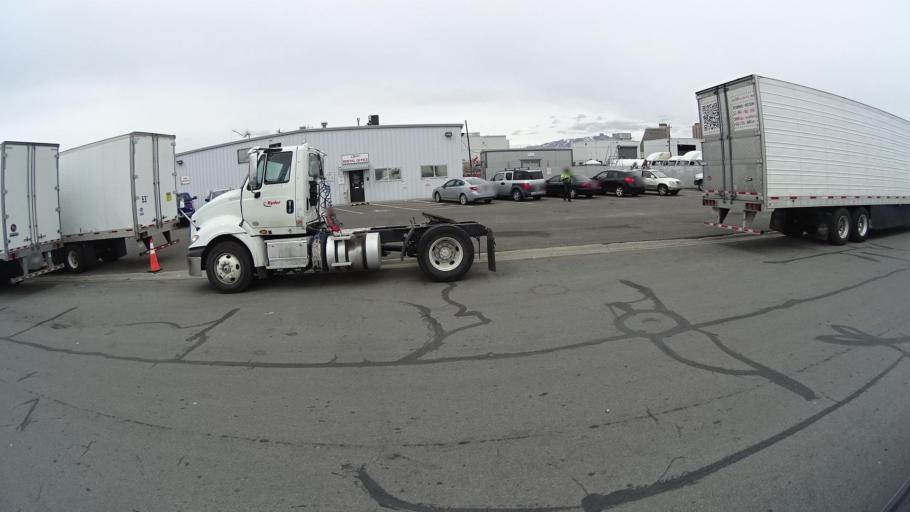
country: US
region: Nevada
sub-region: Washoe County
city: Sparks
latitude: 39.5280
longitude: -119.7484
